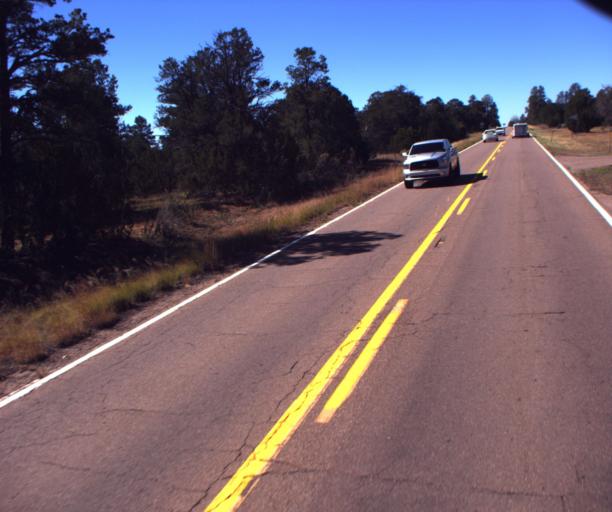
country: US
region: Arizona
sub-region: Navajo County
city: Heber-Overgaard
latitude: 34.4250
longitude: -110.5608
